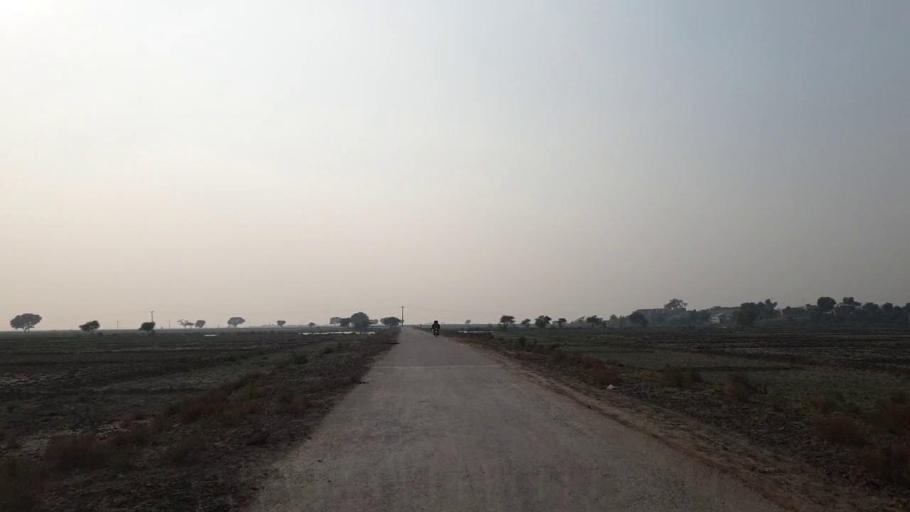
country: PK
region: Sindh
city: Bhan
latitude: 26.4879
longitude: 67.7081
